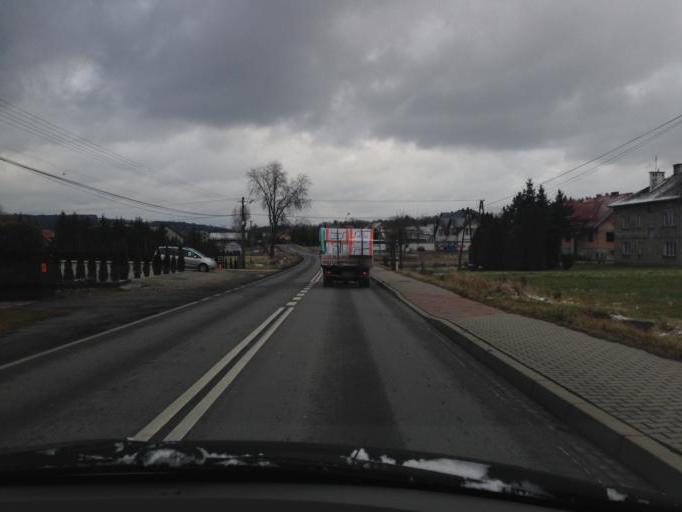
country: PL
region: Lesser Poland Voivodeship
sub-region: Powiat bochenski
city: Lapanow
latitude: 49.8639
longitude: 20.3084
